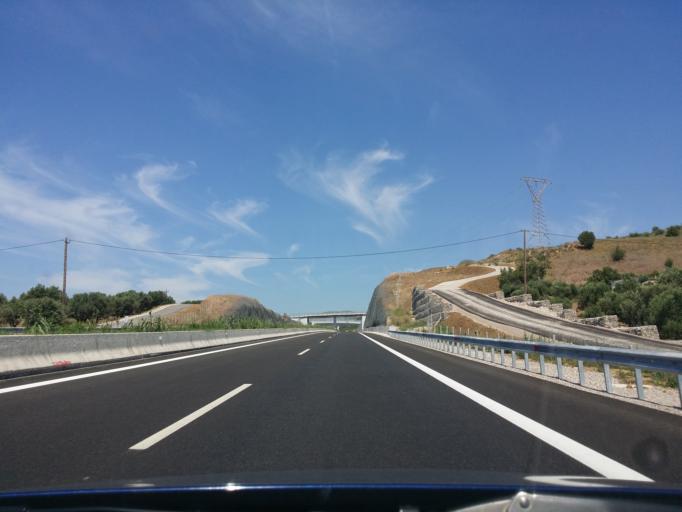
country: GR
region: West Greece
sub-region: Nomos Aitolias kai Akarnanias
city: Mesolongi
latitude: 38.3855
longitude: 21.4858
